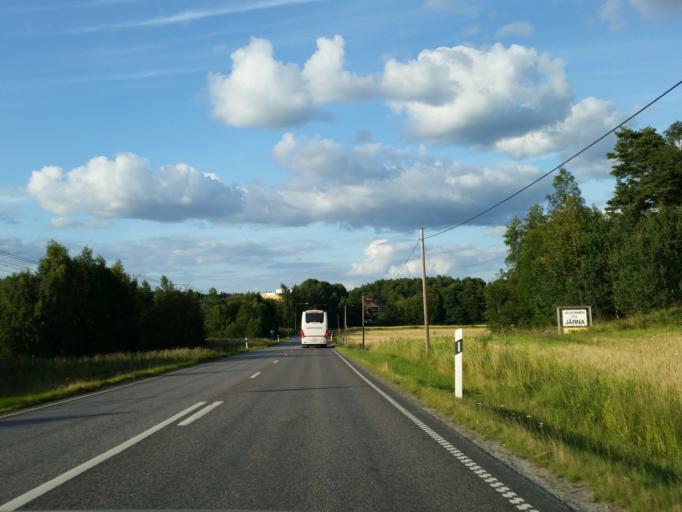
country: SE
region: Stockholm
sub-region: Sodertalje Kommun
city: Pershagen
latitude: 59.0806
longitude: 17.5484
